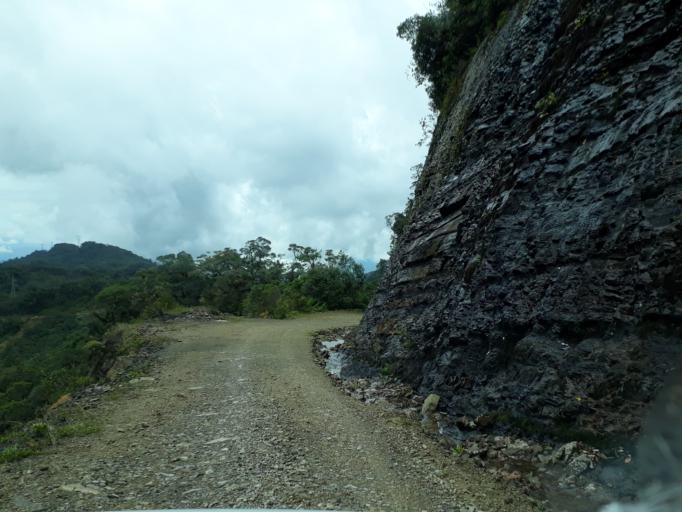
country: CO
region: Cundinamarca
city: Gachala
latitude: 4.7080
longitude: -73.3967
